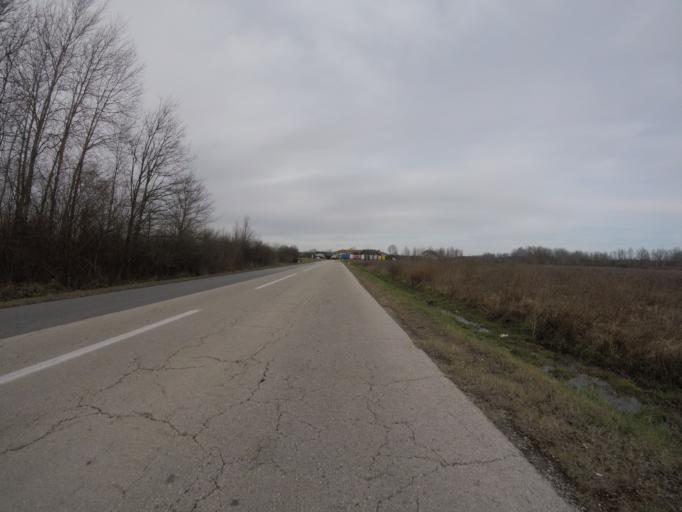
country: HR
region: Grad Zagreb
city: Horvati
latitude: 45.5648
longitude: 15.8632
